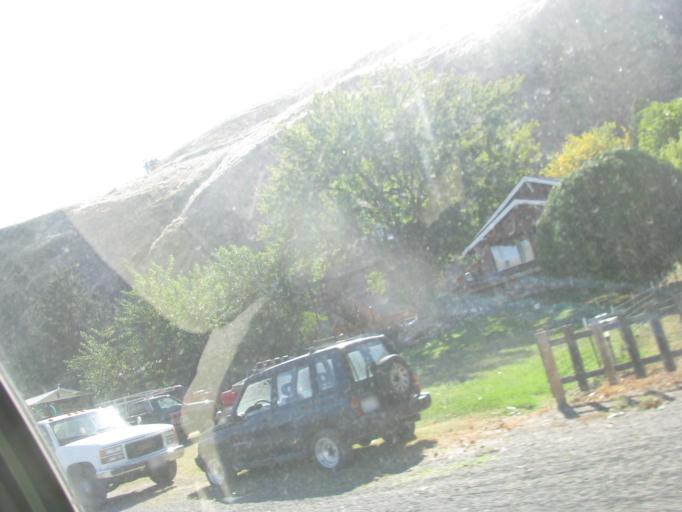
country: US
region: Washington
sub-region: Asotin County
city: Asotin
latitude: 46.3454
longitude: -117.0602
